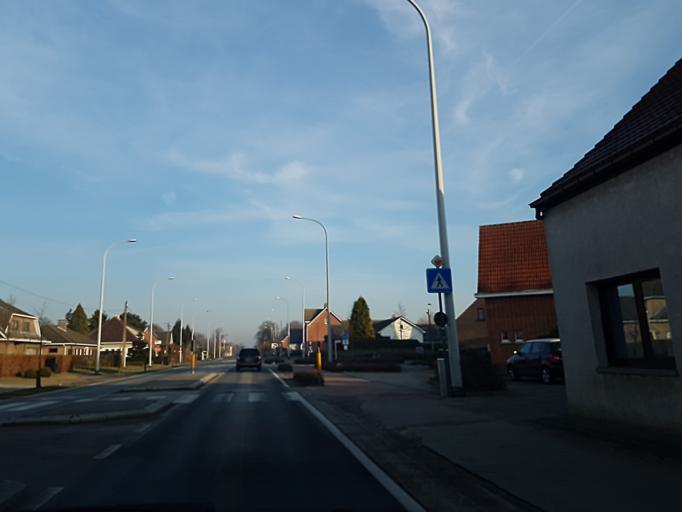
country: BE
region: Flanders
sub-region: Provincie Antwerpen
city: Oostmalle
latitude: 51.3014
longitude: 4.7448
